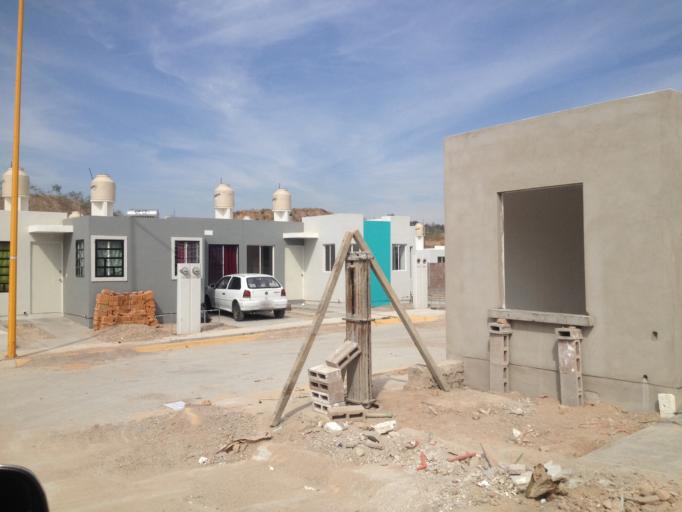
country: MX
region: Aguascalientes
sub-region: Aguascalientes
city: Cumbres III
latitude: 21.8884
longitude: -102.2347
